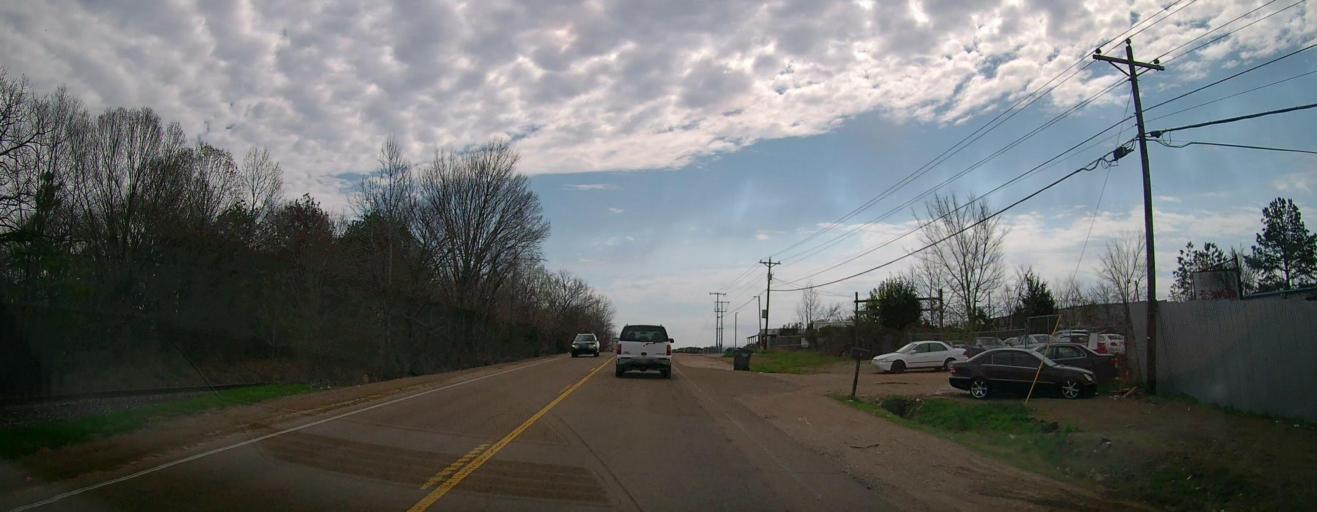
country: US
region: Mississippi
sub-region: Marshall County
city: Byhalia
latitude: 34.8858
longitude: -89.7231
